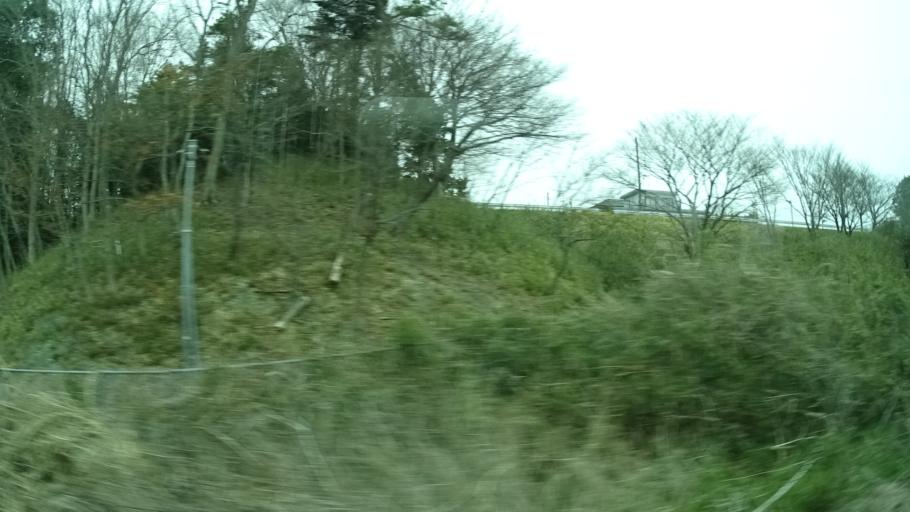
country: JP
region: Fukushima
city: Namie
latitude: 37.3446
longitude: 141.0134
